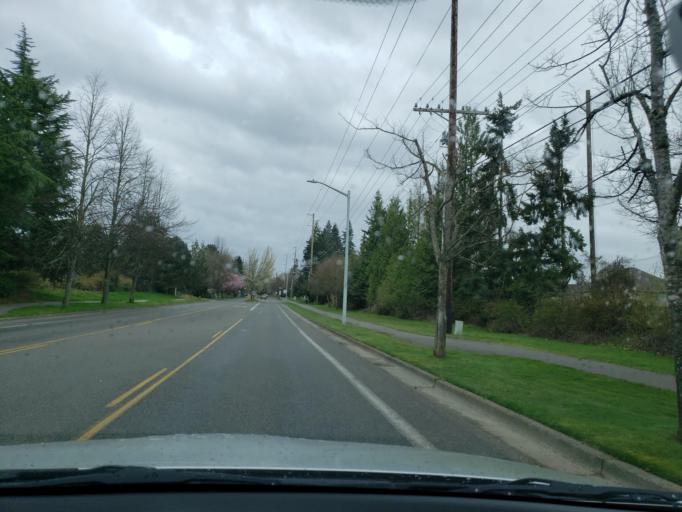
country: US
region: Washington
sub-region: Snohomish County
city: Meadowdale
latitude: 47.8906
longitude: -122.3120
